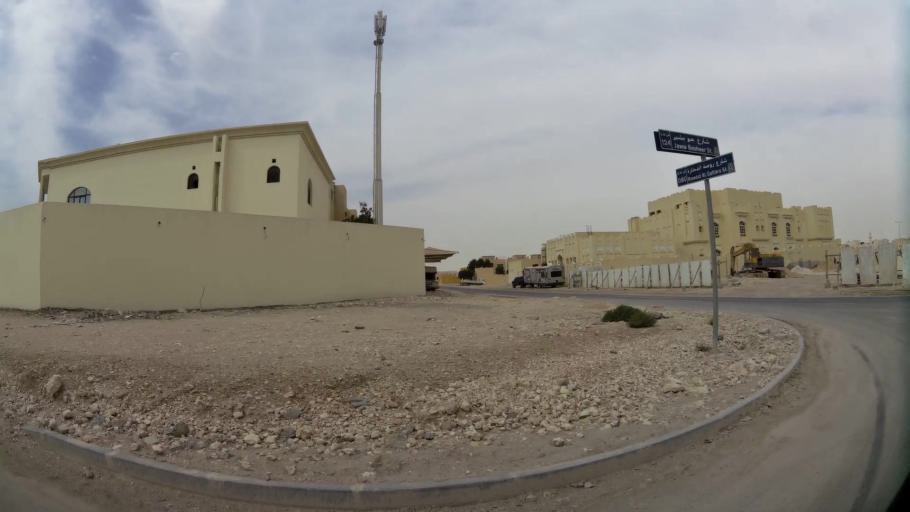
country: QA
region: Baladiyat ad Dawhah
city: Doha
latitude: 25.2163
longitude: 51.4759
